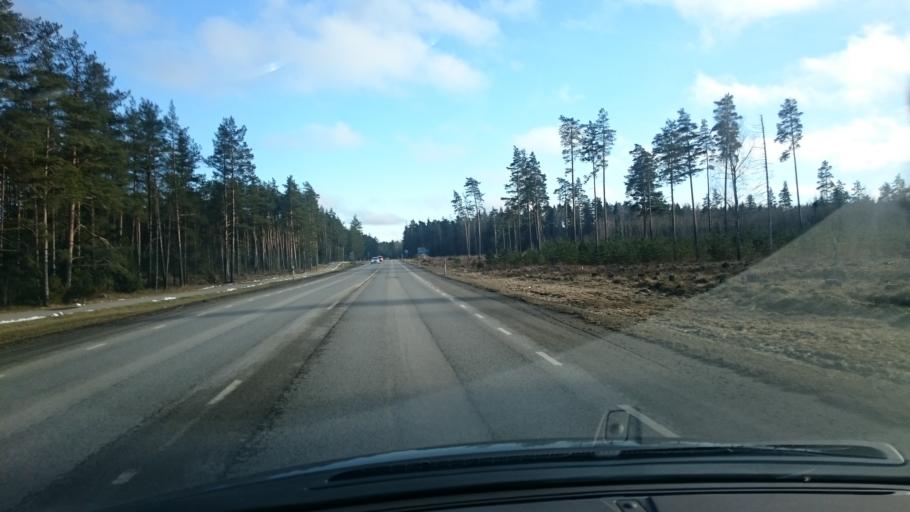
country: EE
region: Harju
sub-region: Tallinna linn
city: Tallinn
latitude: 59.3574
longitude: 24.7698
